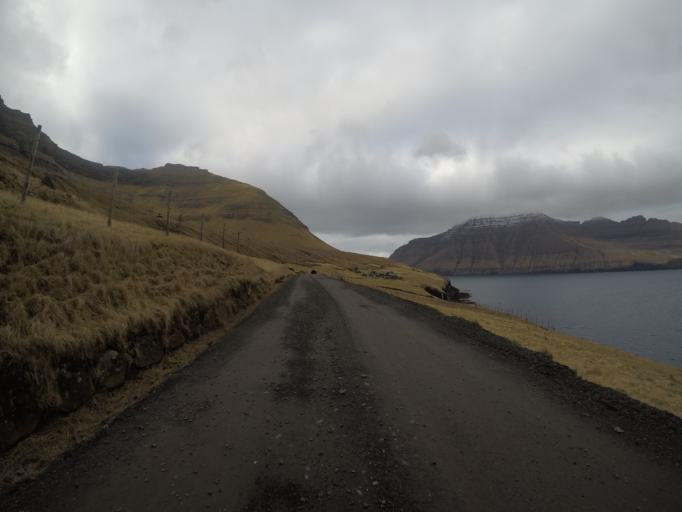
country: FO
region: Nordoyar
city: Klaksvik
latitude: 62.3475
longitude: -6.5812
